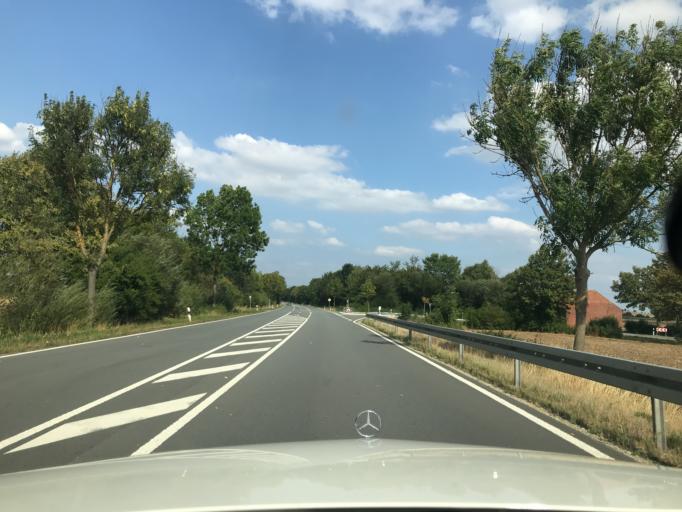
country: DE
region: North Rhine-Westphalia
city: Borgentreich
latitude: 51.5459
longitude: 9.2105
